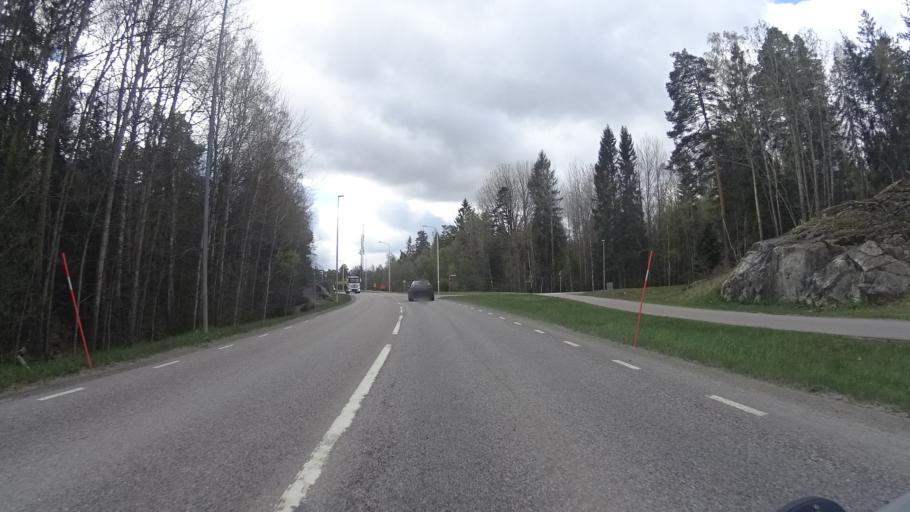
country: SE
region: Stockholm
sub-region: Botkyrka Kommun
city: Tullinge
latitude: 59.2029
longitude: 17.9251
